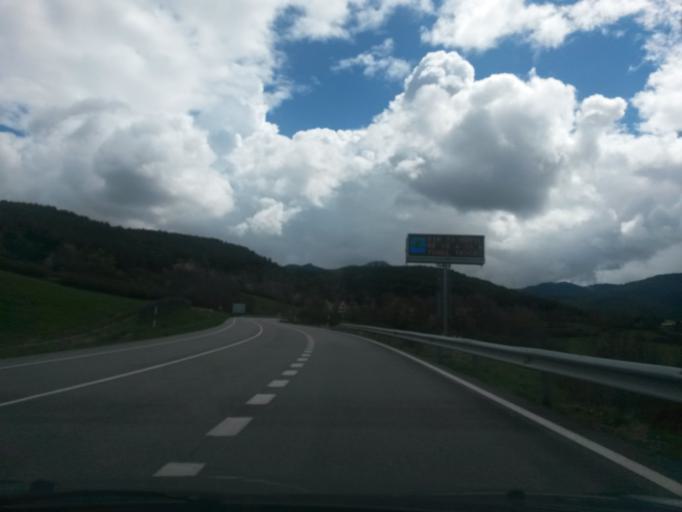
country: ES
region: Catalonia
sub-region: Provincia de Girona
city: Isovol
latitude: 42.3600
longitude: 1.8136
